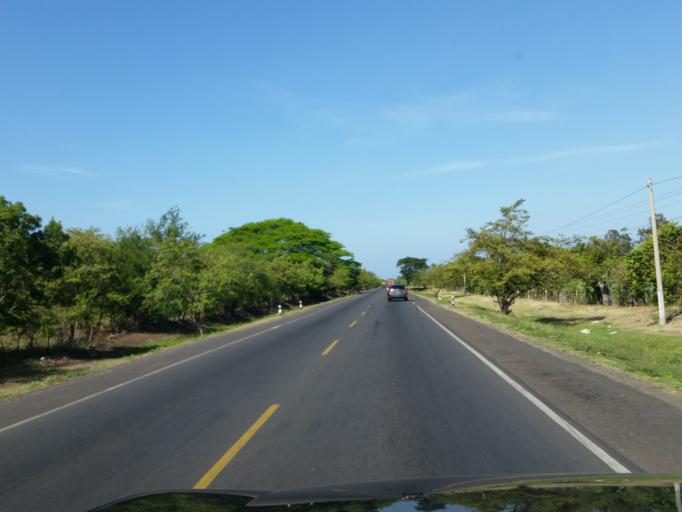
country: NI
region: Leon
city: La Paz Centro
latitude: 12.3199
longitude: -86.6935
